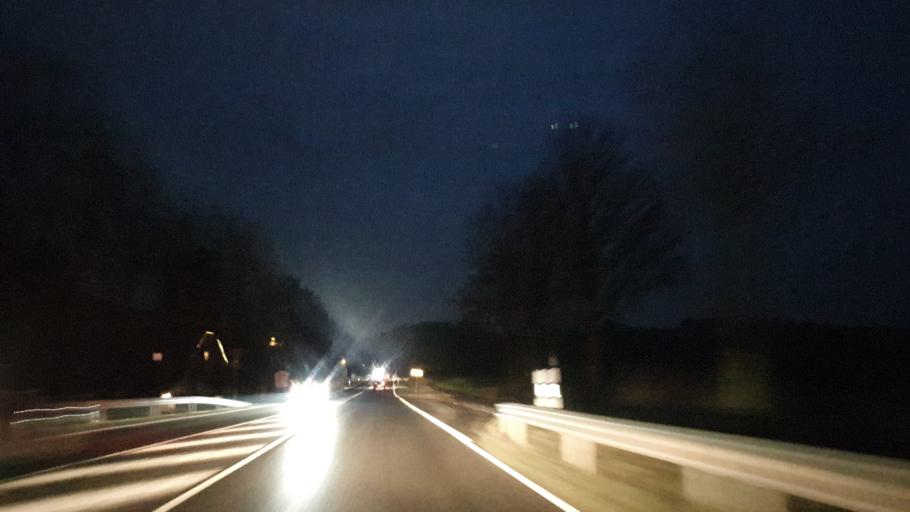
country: DE
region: Rheinland-Pfalz
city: Dernbach
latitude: 50.4575
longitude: 7.8056
